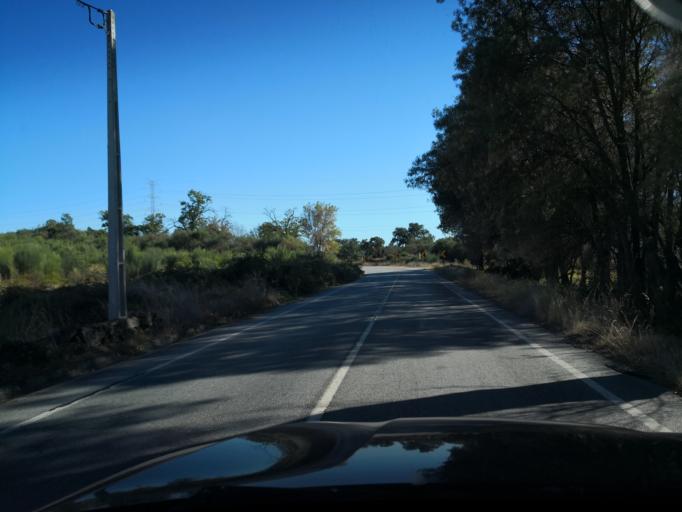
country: PT
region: Vila Real
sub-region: Valpacos
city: Valpacos
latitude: 41.6460
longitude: -7.3201
